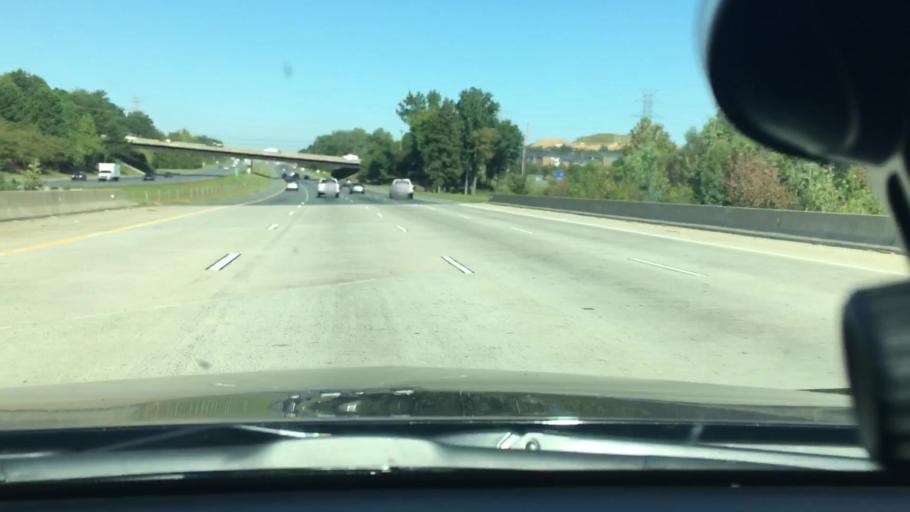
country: US
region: North Carolina
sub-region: Cabarrus County
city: Harrisburg
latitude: 35.3313
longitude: -80.7193
